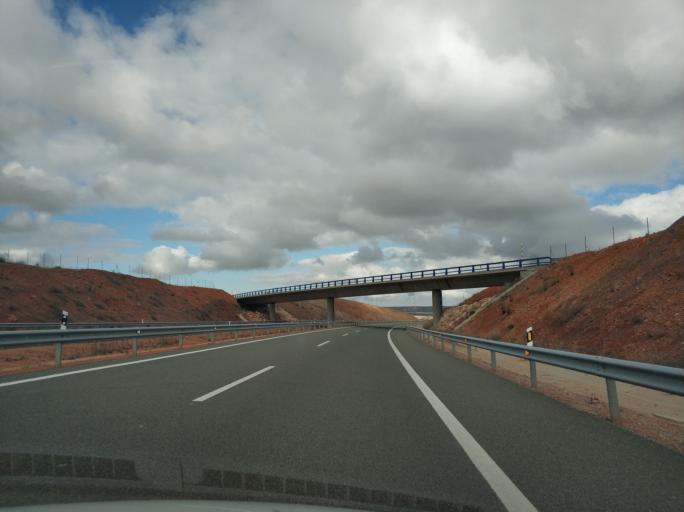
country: ES
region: Castille and Leon
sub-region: Provincia de Soria
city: Yelo
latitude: 41.2399
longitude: -2.4791
